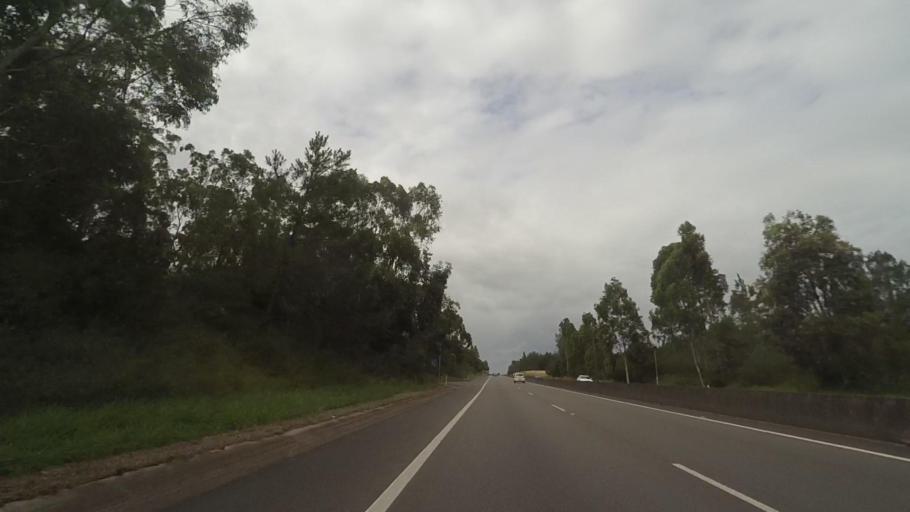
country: AU
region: New South Wales
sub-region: Port Stephens Shire
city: Raymond Terrace
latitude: -32.7661
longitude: 151.7629
